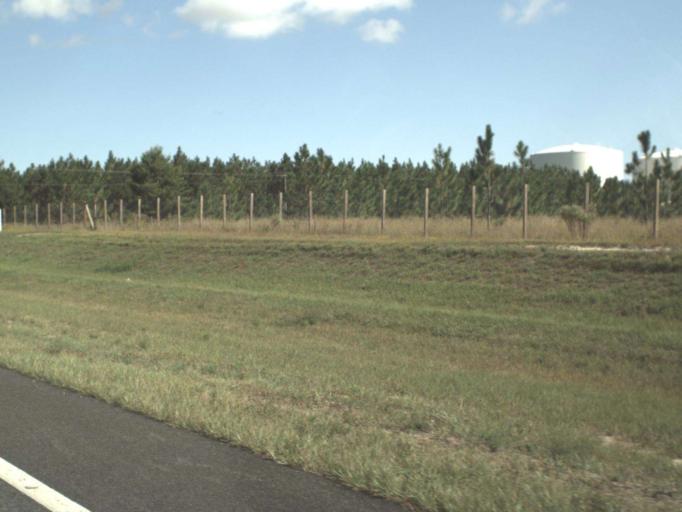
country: US
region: Florida
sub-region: Walton County
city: Freeport
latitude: 30.5728
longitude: -86.1079
